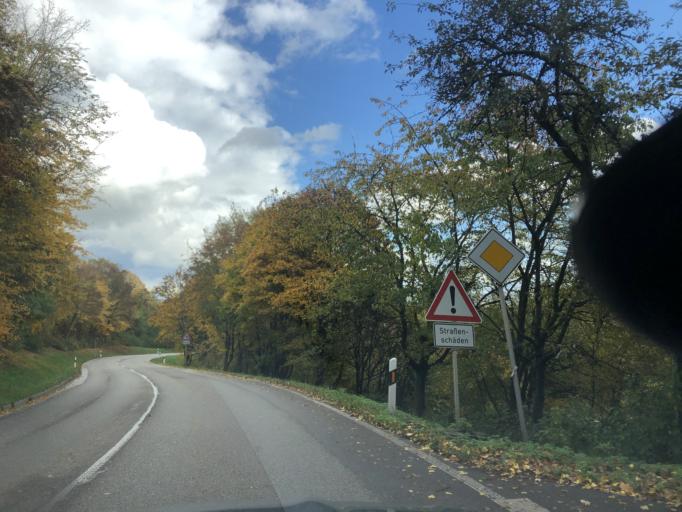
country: DE
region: Baden-Wuerttemberg
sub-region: Regierungsbezirk Stuttgart
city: Winterbach
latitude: 48.7913
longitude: 9.4691
